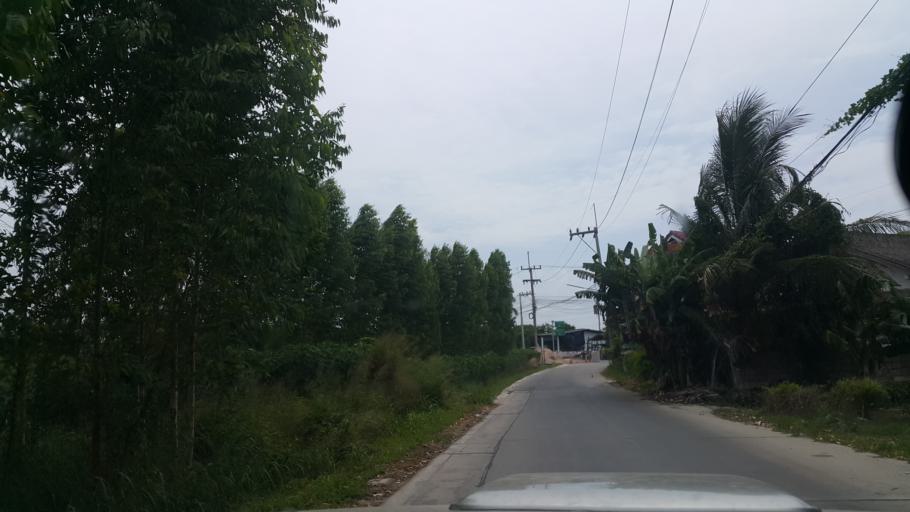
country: TH
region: Rayong
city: Ban Chang
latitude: 12.7182
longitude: 101.0649
